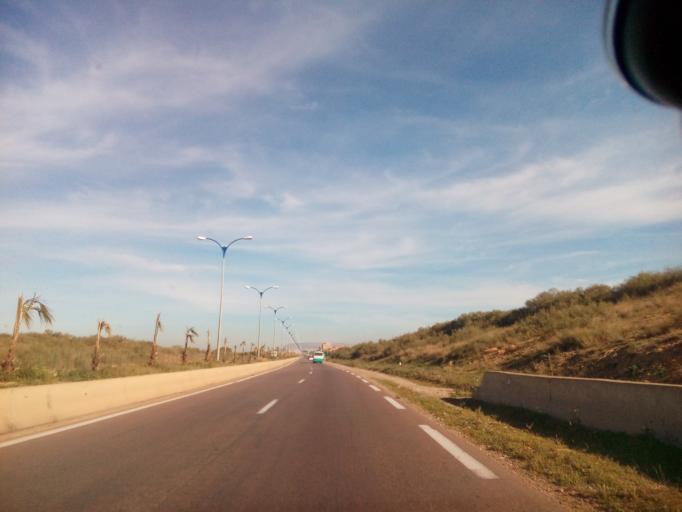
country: DZ
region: Mostaganem
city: Mostaganem
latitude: 35.8597
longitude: 0.0312
